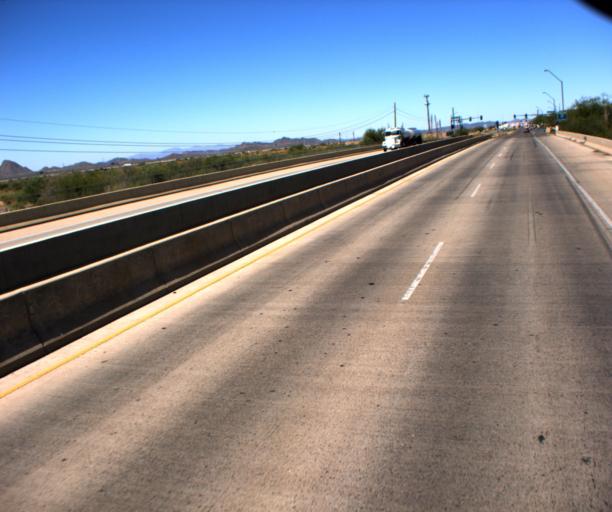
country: US
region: Arizona
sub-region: Maricopa County
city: Anthem
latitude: 33.7984
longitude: -112.1234
